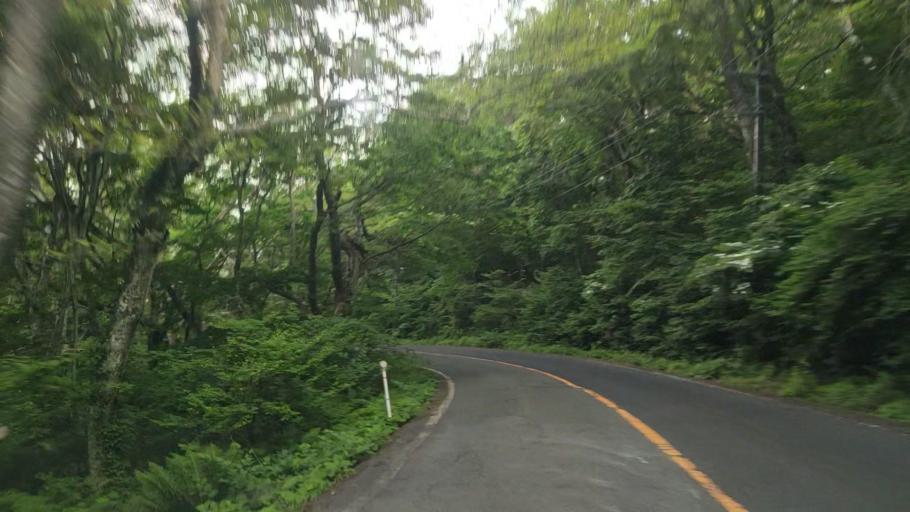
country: JP
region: Tottori
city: Yonago
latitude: 35.3637
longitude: 133.5229
